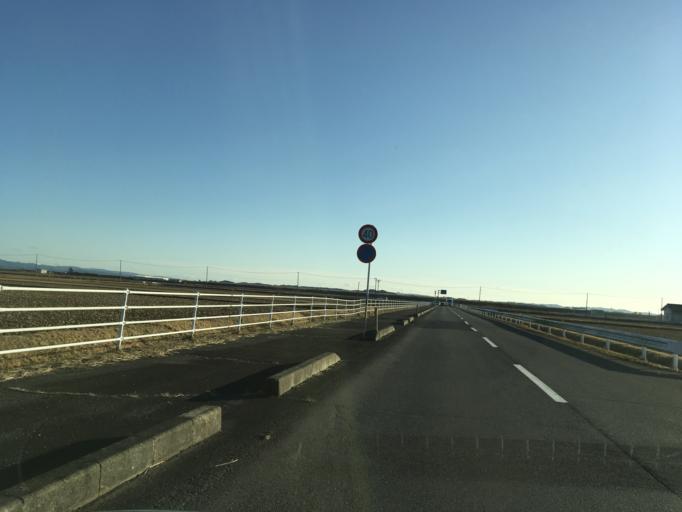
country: JP
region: Iwate
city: Ichinoseki
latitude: 38.7497
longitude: 141.1644
